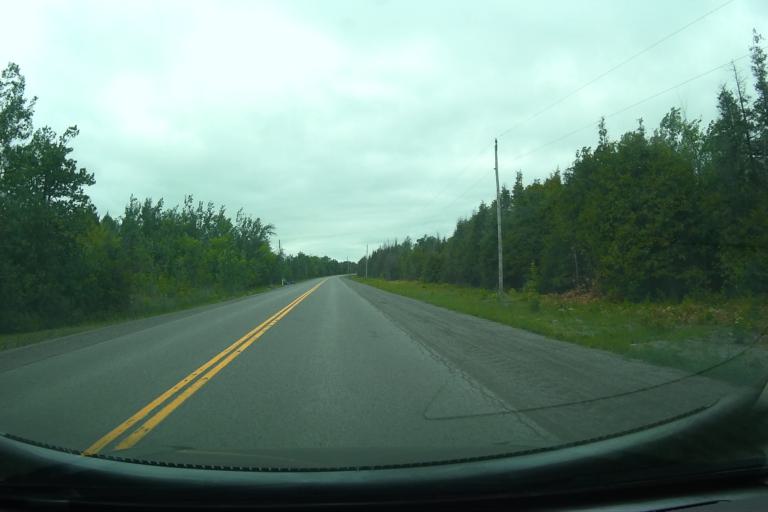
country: CA
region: Ontario
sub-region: Lanark County
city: Smiths Falls
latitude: 45.0270
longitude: -75.8584
